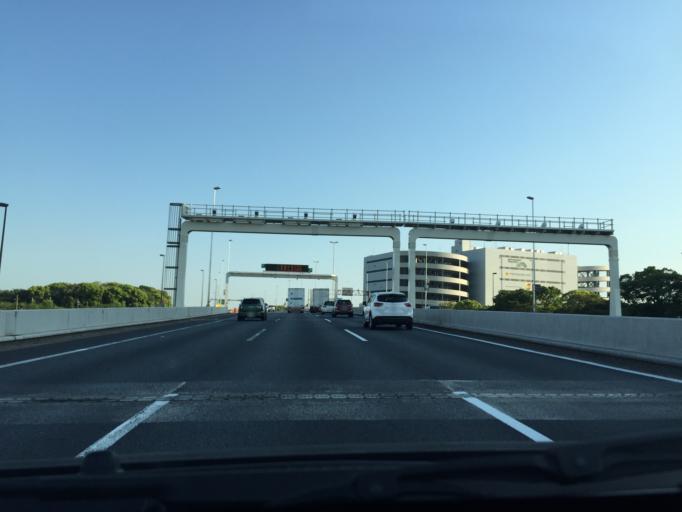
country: JP
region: Kanagawa
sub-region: Kawasaki-shi
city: Kawasaki
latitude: 35.5867
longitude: 139.7555
